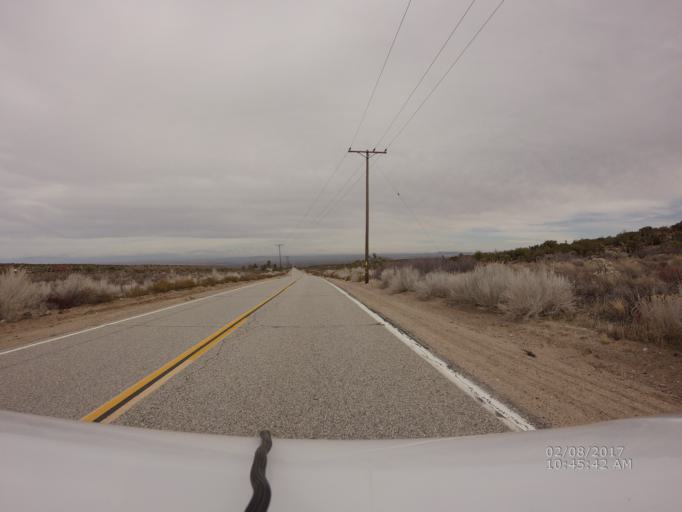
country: US
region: California
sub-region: San Bernardino County
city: Pinon Hills
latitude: 34.4428
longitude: -117.7649
